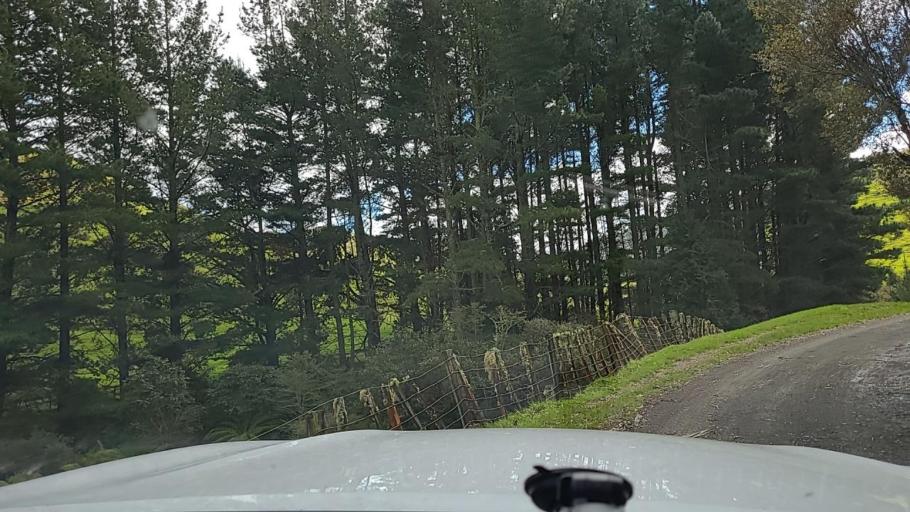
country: NZ
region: Bay of Plenty
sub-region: Opotiki District
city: Opotiki
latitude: -38.2138
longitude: 177.5904
